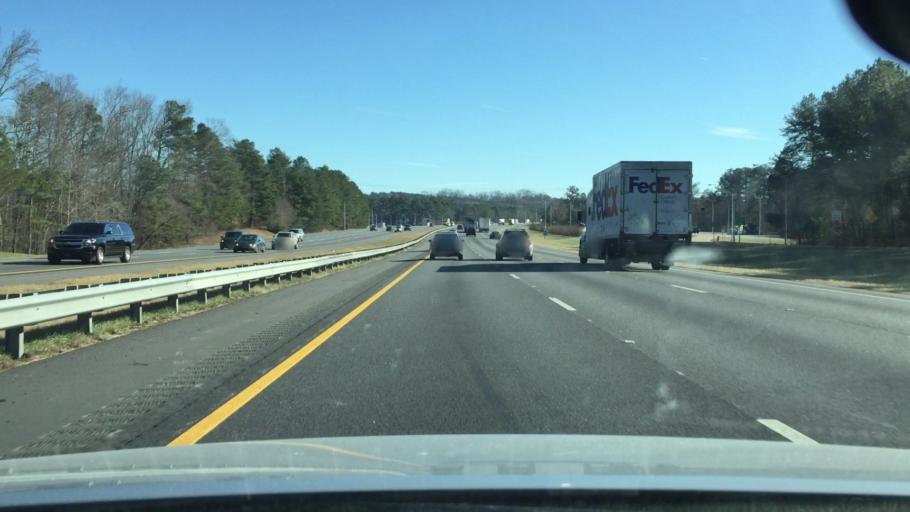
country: US
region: Georgia
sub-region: Catoosa County
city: Ringgold
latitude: 34.8826
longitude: -85.0551
